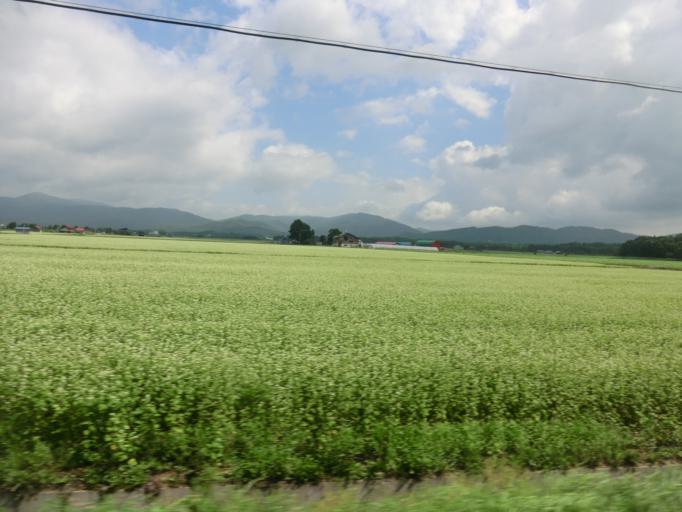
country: JP
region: Hokkaido
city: Fukagawa
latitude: 43.9893
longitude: 142.1421
